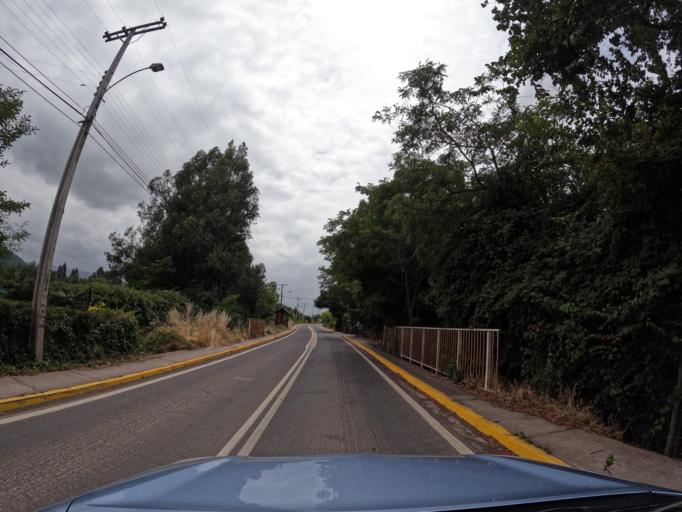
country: CL
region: Maule
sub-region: Provincia de Curico
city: Teno
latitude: -34.7776
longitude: -71.1719
